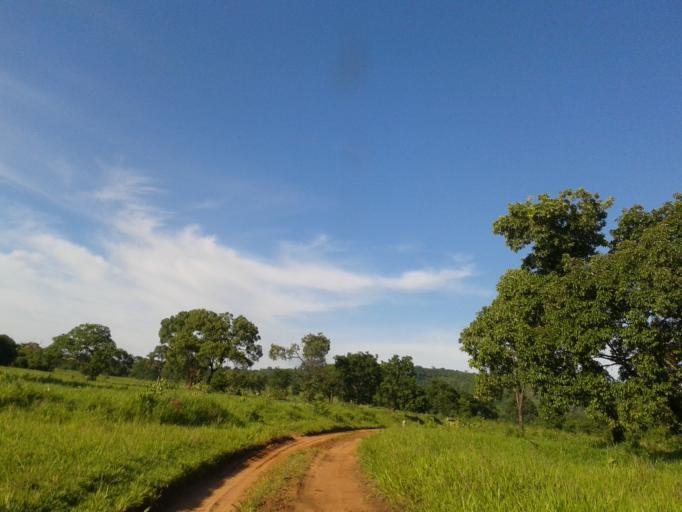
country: BR
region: Minas Gerais
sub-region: Santa Vitoria
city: Santa Vitoria
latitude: -19.0820
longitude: -49.9580
